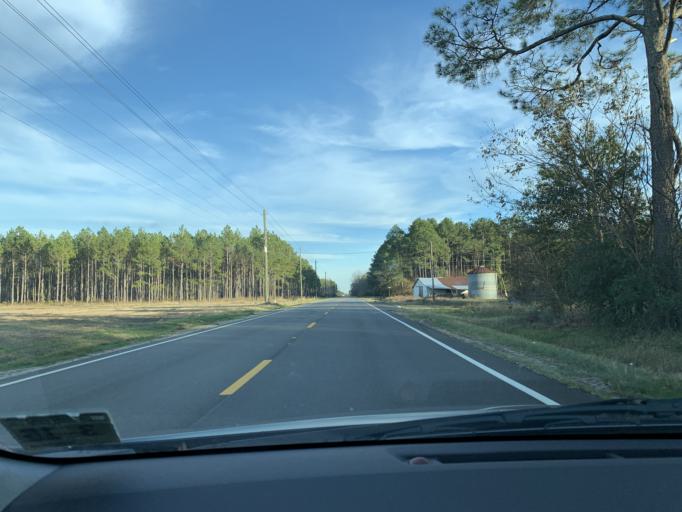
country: US
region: Georgia
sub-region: Irwin County
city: Ocilla
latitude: 31.5844
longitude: -83.0744
